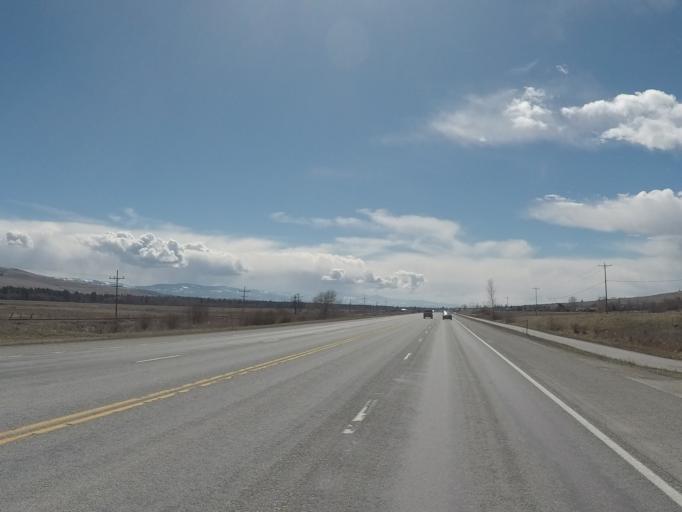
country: US
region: Montana
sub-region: Missoula County
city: Lolo
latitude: 46.7336
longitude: -114.0801
